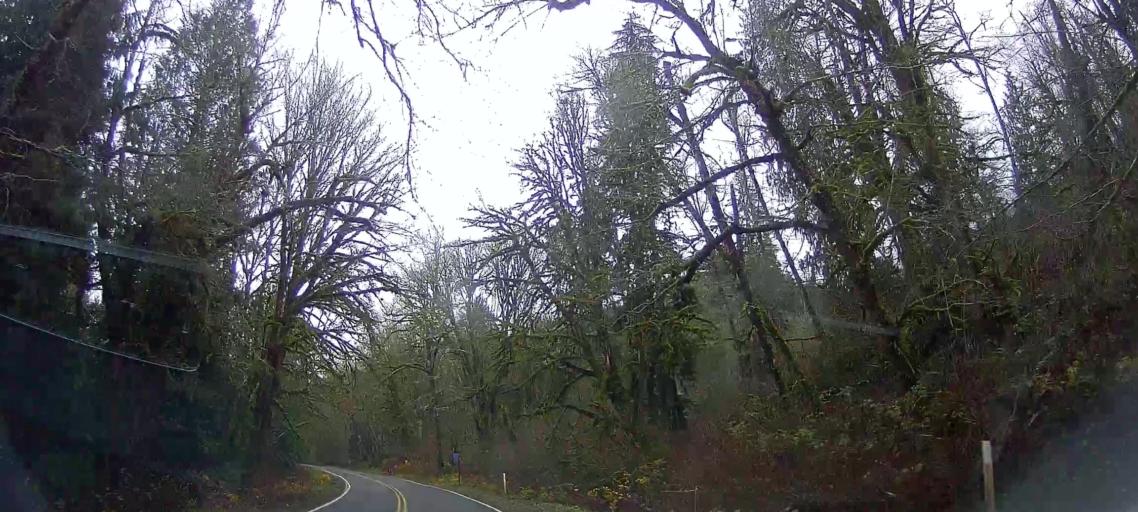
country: US
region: Washington
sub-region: Skagit County
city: Sedro-Woolley
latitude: 48.5089
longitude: -121.8957
